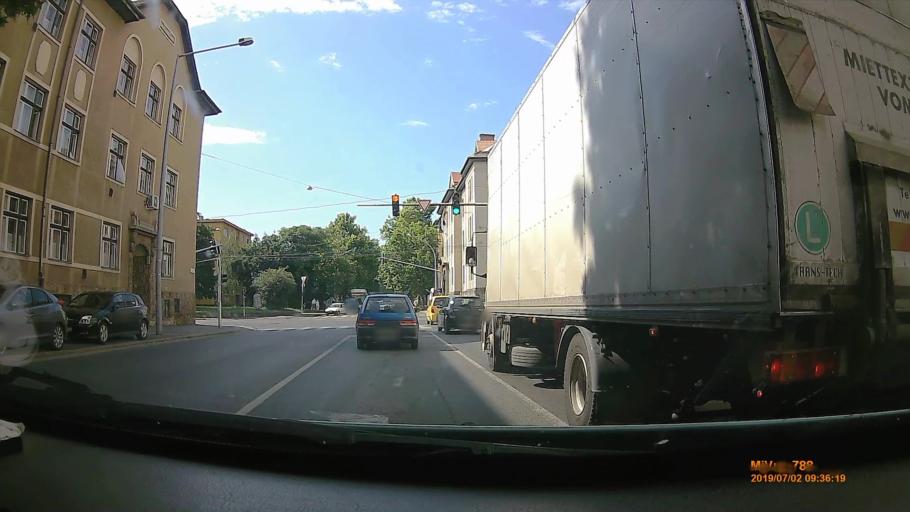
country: HU
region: Borsod-Abauj-Zemplen
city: Miskolc
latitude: 48.1032
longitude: 20.7980
